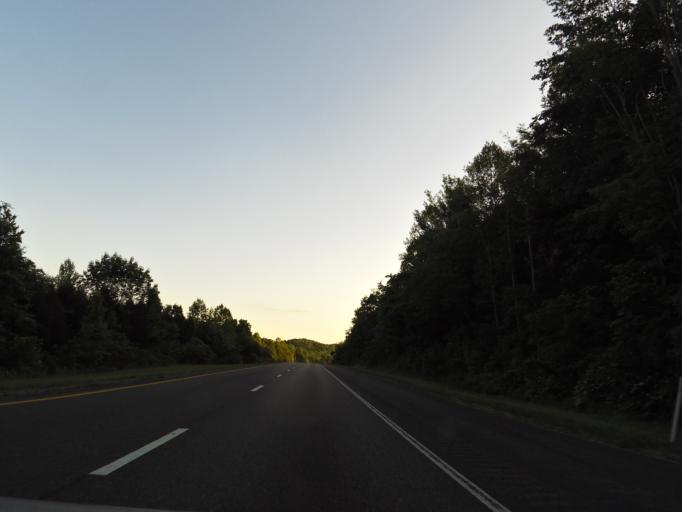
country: US
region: Tennessee
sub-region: Washington County
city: Fall Branch
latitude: 36.3771
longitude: -82.6707
